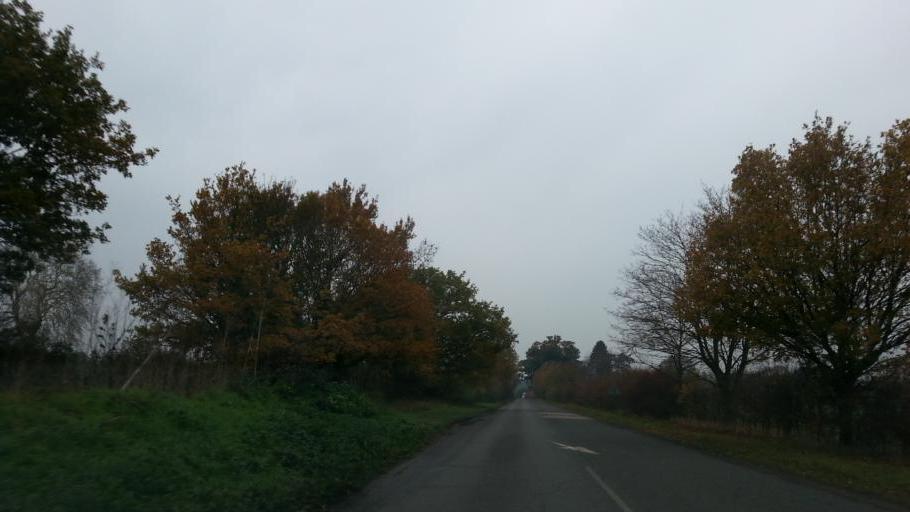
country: GB
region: England
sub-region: Suffolk
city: Thurston
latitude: 52.2335
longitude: 0.8041
